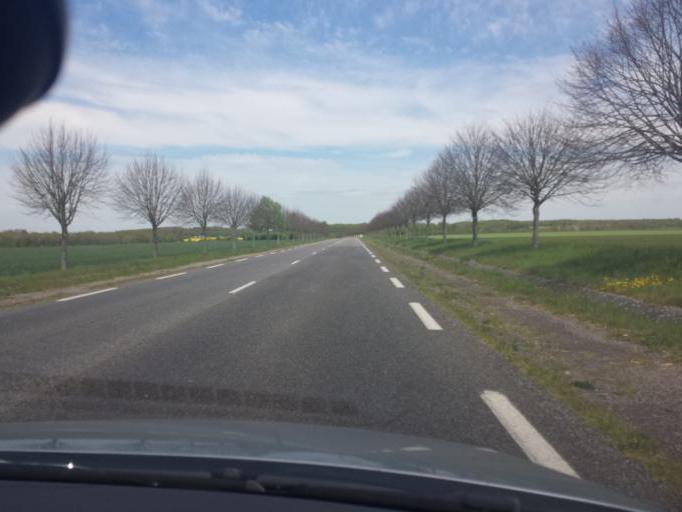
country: FR
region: Haute-Normandie
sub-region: Departement de l'Eure
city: Breteuil
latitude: 48.8289
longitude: 0.9334
